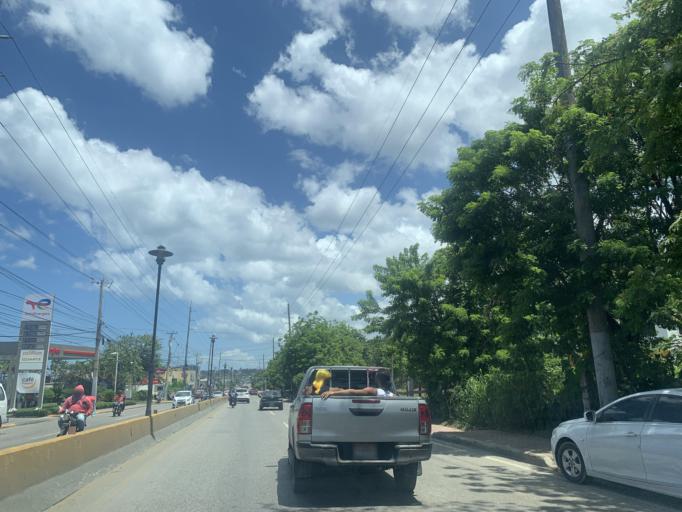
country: DO
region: Puerto Plata
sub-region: Puerto Plata
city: Puerto Plata
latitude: 19.7935
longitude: -70.7107
